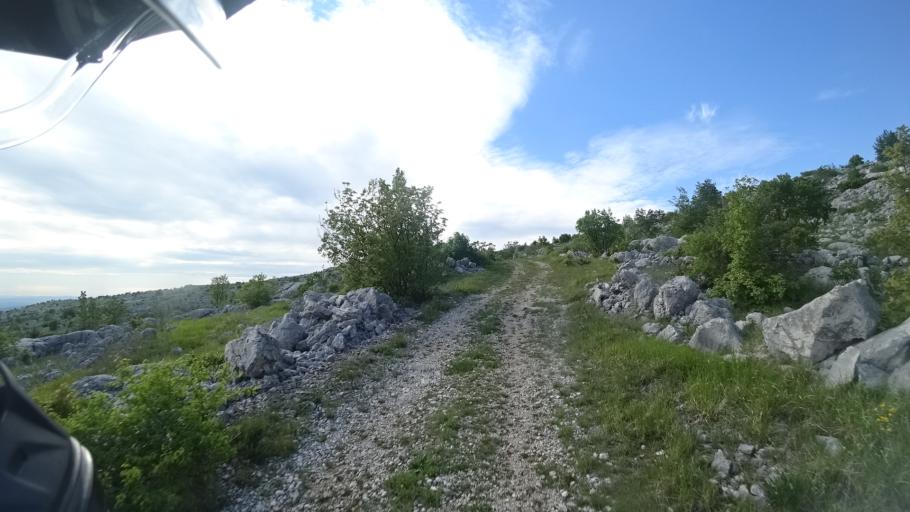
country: HR
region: Splitsko-Dalmatinska
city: Hrvace
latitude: 43.7992
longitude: 16.4339
